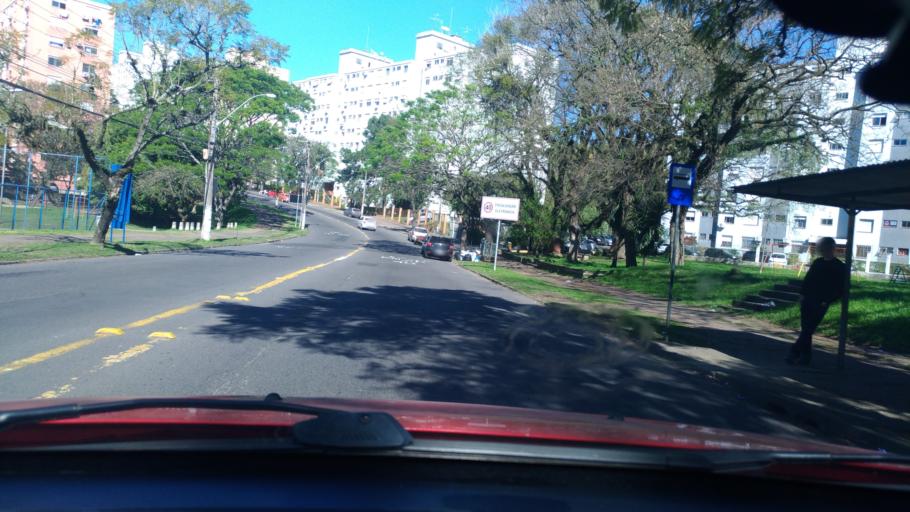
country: BR
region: Rio Grande do Sul
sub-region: Porto Alegre
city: Porto Alegre
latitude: -30.0379
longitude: -51.1445
